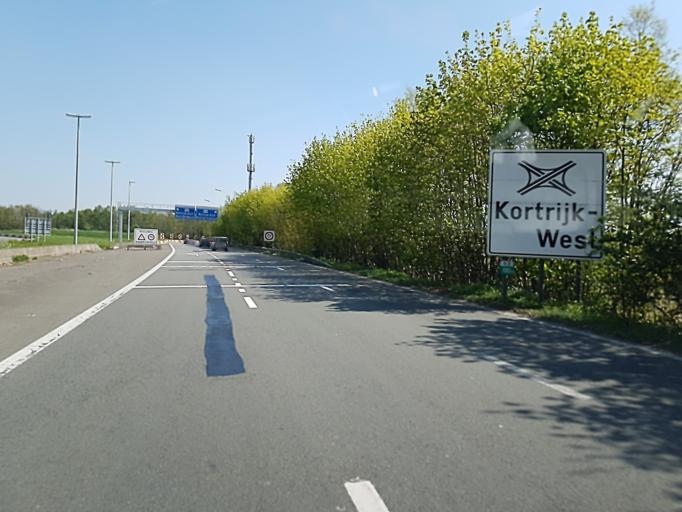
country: BE
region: Flanders
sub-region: Provincie West-Vlaanderen
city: Wevelgem
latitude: 50.8282
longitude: 3.2107
